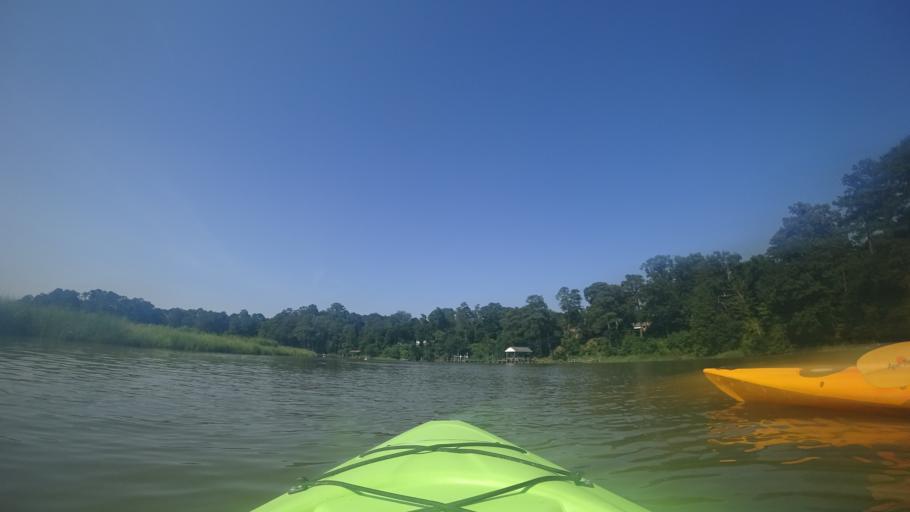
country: US
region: Virginia
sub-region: Isle of Wight County
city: Smithfield
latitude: 36.9667
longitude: -76.6126
